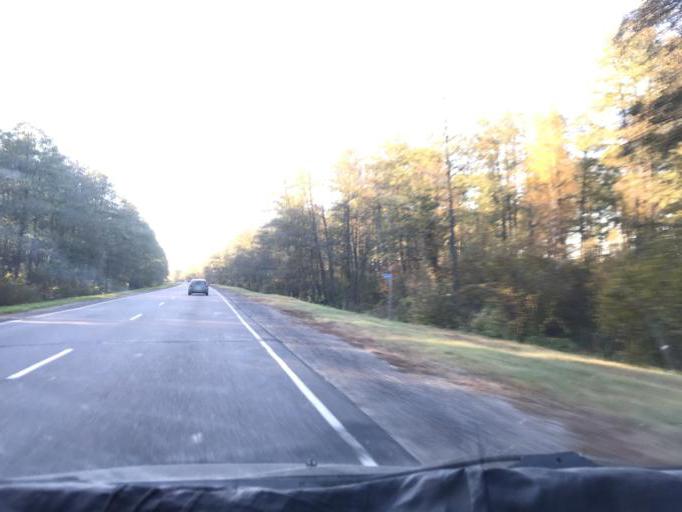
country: BY
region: Gomel
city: Pyetrykaw
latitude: 52.2736
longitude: 28.2574
